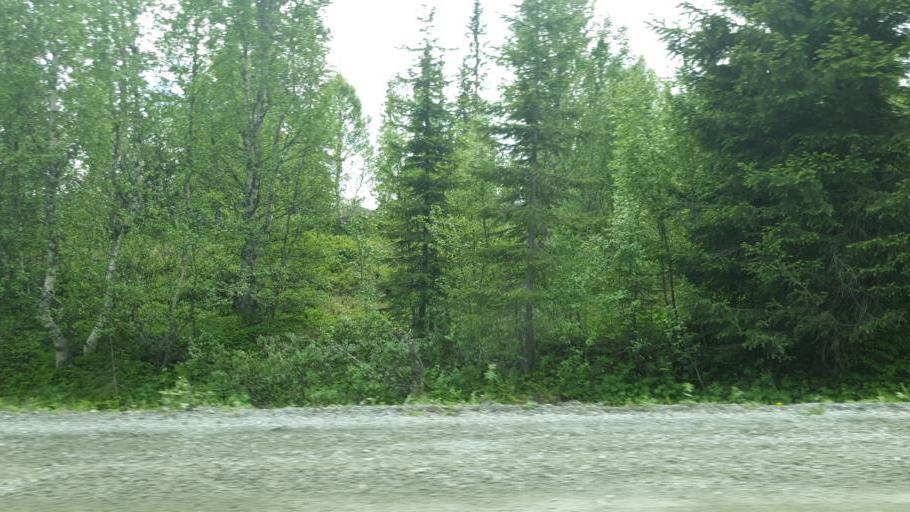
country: NO
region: Nord-Trondelag
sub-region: Leksvik
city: Leksvik
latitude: 63.6870
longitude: 10.3976
